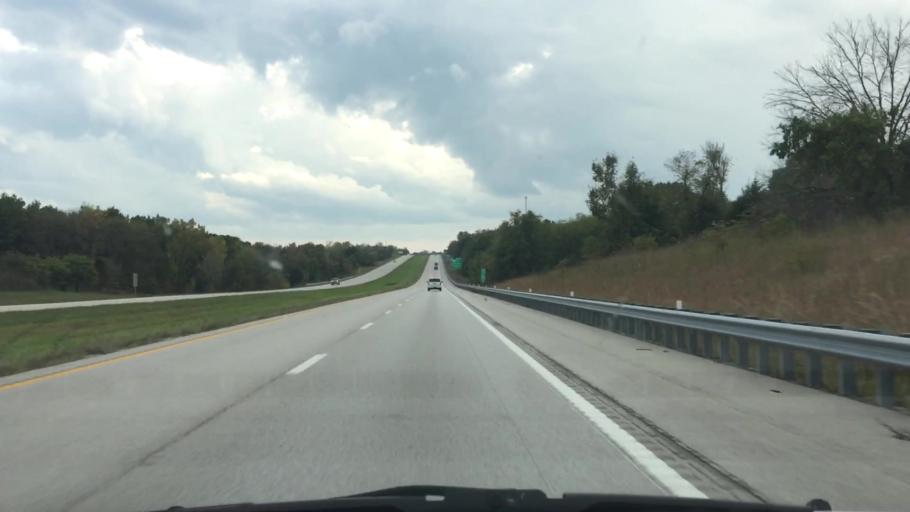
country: US
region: Missouri
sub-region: Clinton County
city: Cameron
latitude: 39.7736
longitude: -94.2124
